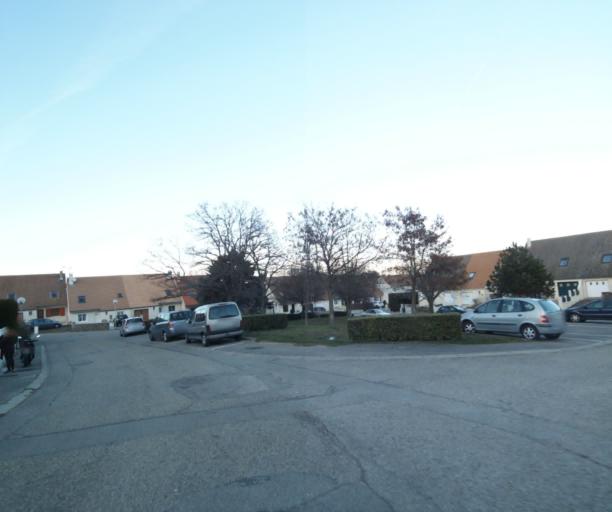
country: FR
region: Rhone-Alpes
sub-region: Departement de l'Ardeche
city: Davezieux
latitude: 45.2538
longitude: 4.7130
